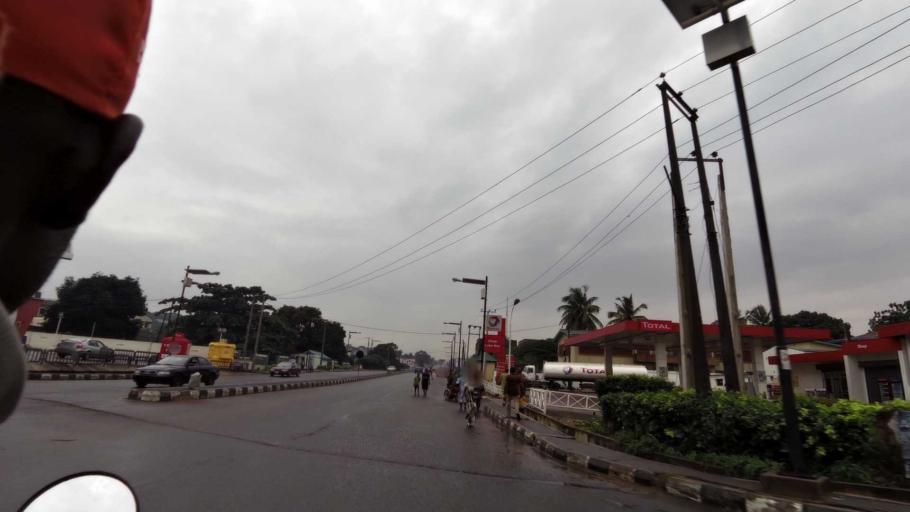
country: NG
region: Oyo
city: Ibadan
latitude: 7.3983
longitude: 3.9092
